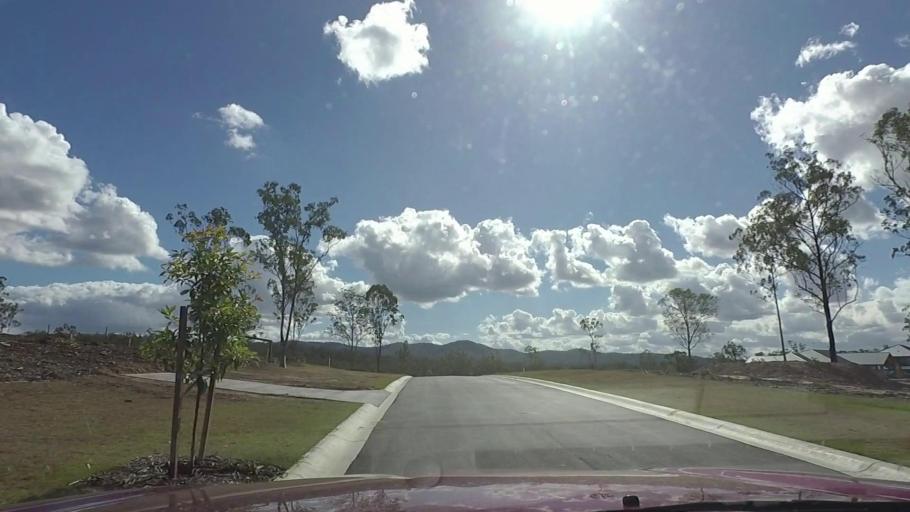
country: AU
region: Queensland
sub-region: Ipswich
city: Springfield Lakes
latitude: -27.7571
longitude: 152.9213
